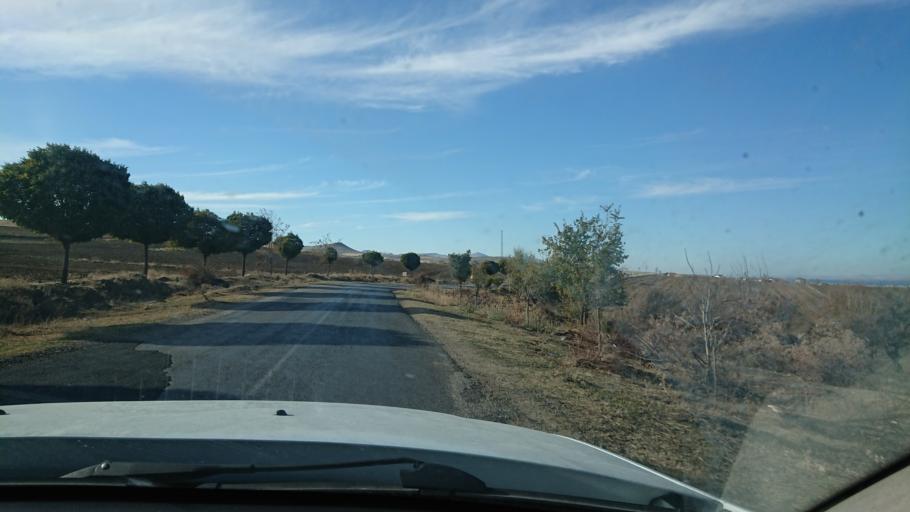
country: TR
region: Aksaray
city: Sariyahsi
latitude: 38.9728
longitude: 33.8607
